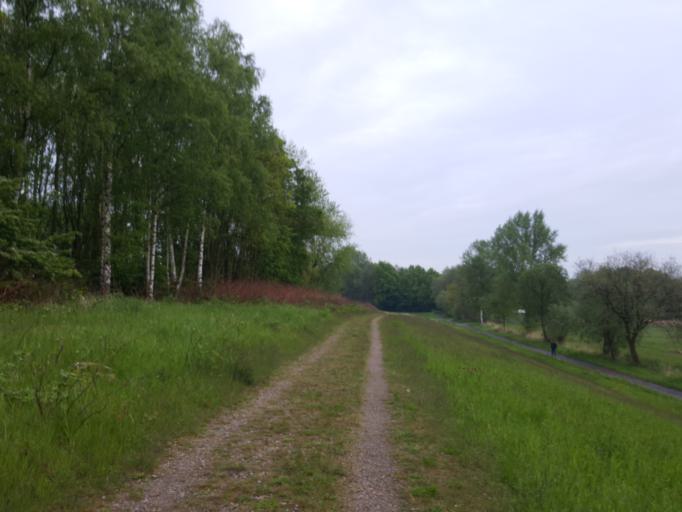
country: DE
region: Schleswig-Holstein
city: Oststeinbek
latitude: 53.5222
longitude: 10.1306
